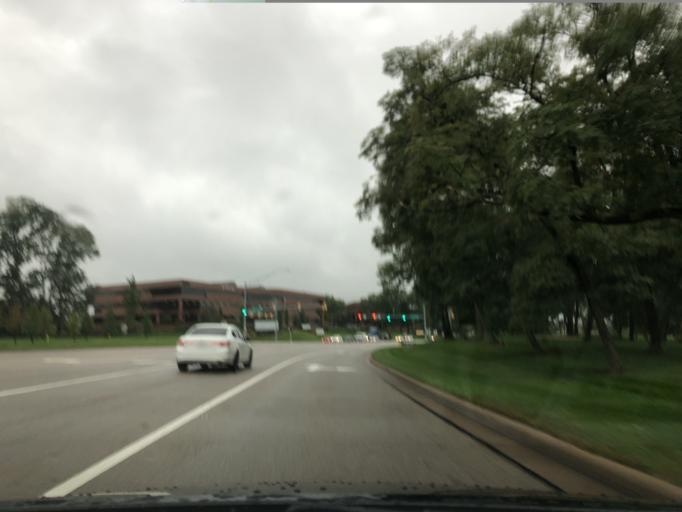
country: US
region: Ohio
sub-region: Hamilton County
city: Blue Ash
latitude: 39.2469
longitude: -84.3807
